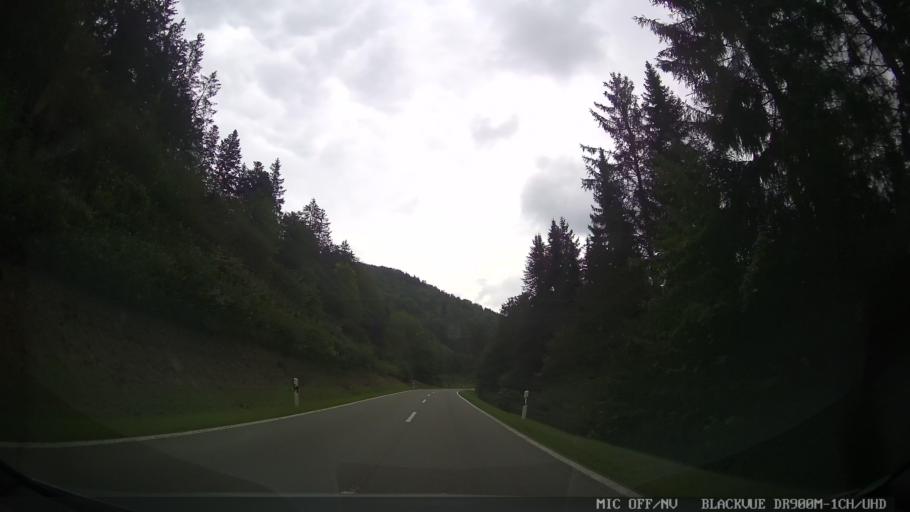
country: DE
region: Baden-Wuerttemberg
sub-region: Freiburg Region
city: Barenthal
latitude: 48.0906
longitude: 8.9249
